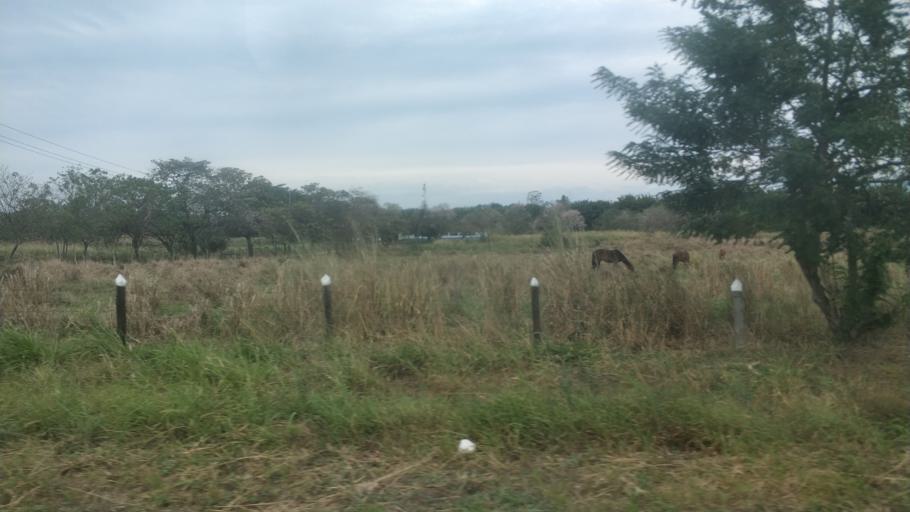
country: BR
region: Rio de Janeiro
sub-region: Seropedica
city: Seropedica
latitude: -22.7731
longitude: -43.6683
